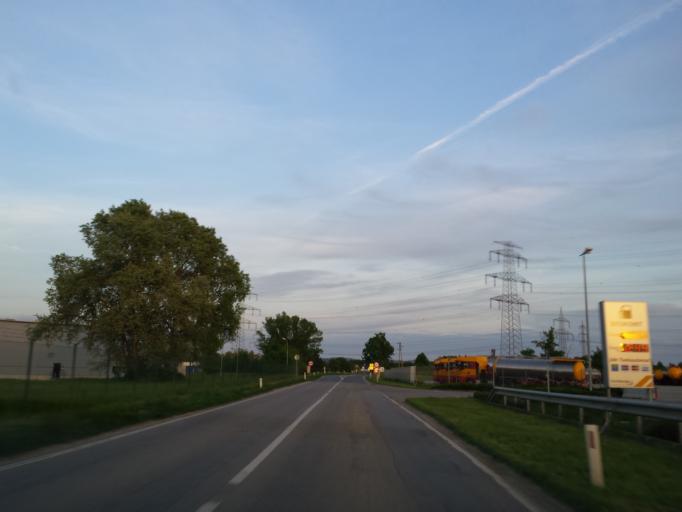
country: AT
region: Lower Austria
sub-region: Politischer Bezirk Tulln
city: Michelhausen
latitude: 48.3341
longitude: 15.9420
